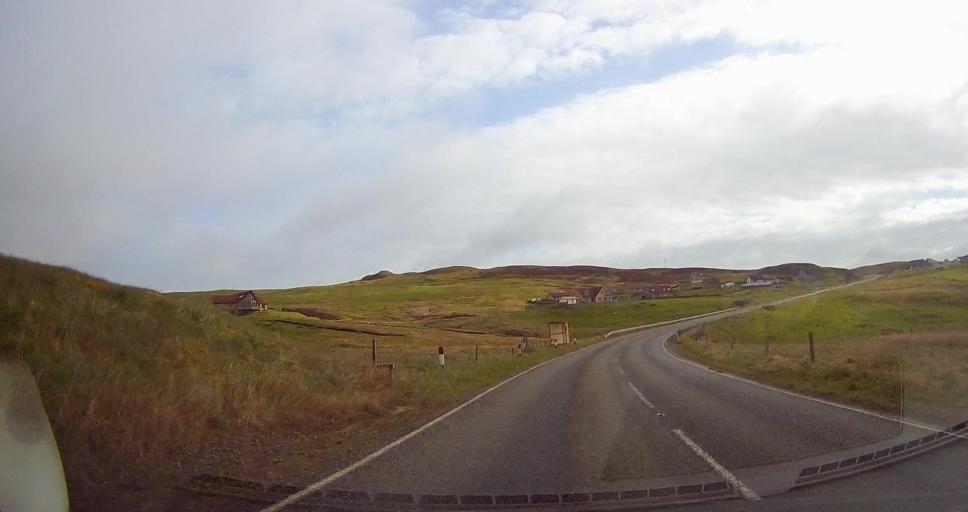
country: GB
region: Scotland
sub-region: Shetland Islands
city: Lerwick
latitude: 60.1030
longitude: -1.2329
